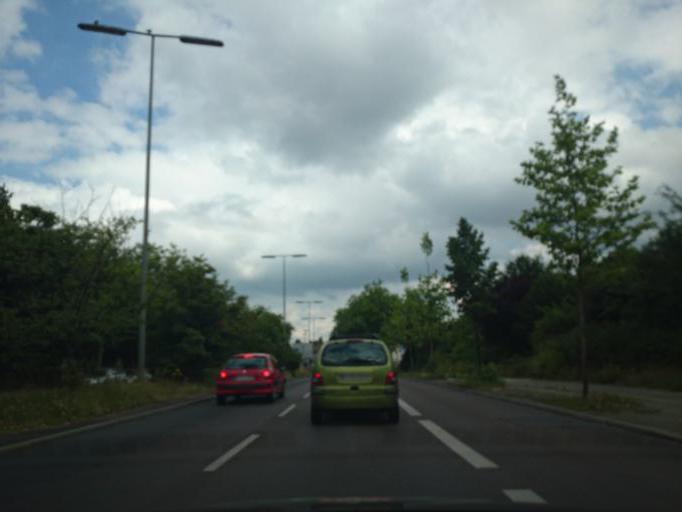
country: DE
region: Berlin
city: Marienfelde
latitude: 52.4115
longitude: 13.3644
